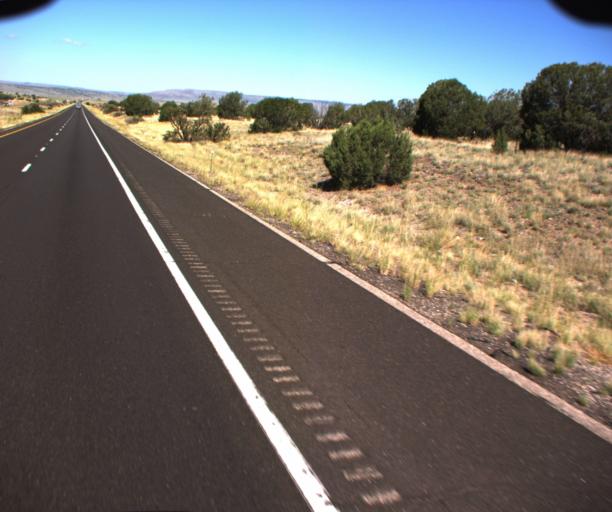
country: US
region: Arizona
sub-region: Yavapai County
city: Paulden
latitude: 35.2827
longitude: -112.7924
